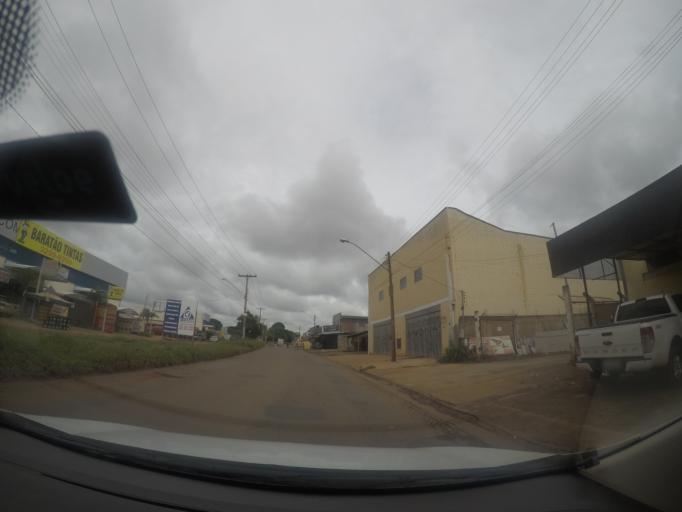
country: BR
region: Goias
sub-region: Goiania
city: Goiania
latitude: -16.6851
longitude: -49.3732
